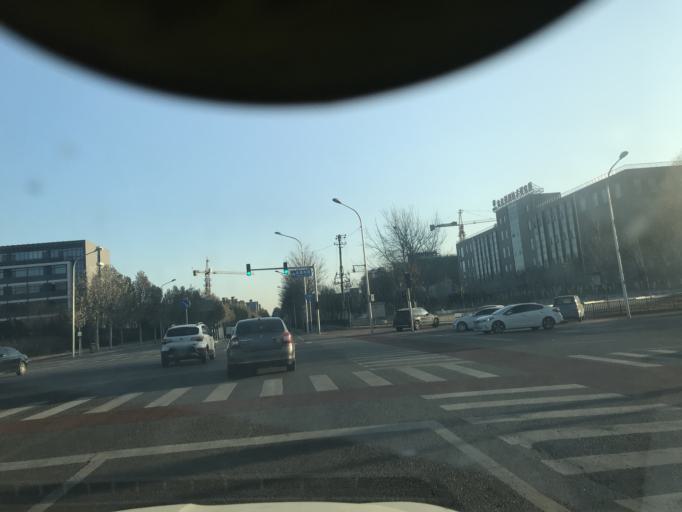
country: CN
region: Beijing
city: Xibeiwang
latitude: 40.0722
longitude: 116.2454
